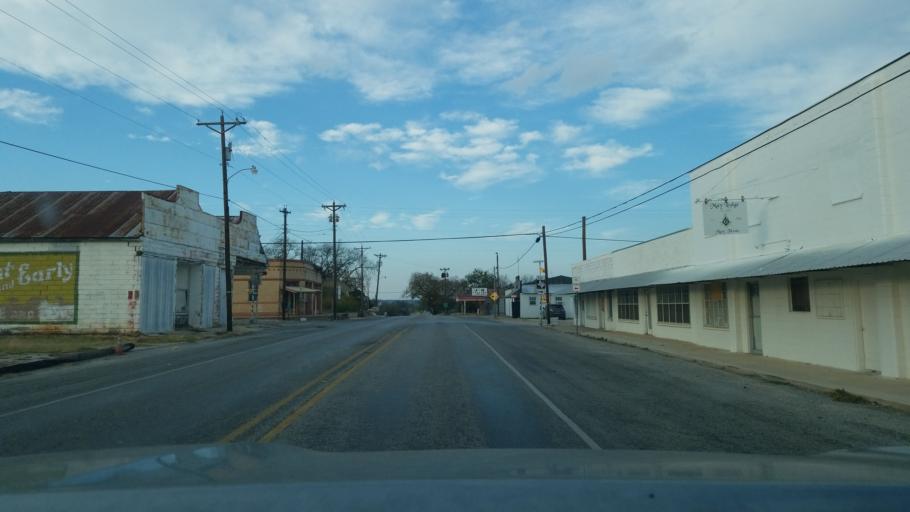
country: US
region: Texas
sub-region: Brown County
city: Lake Brownwood
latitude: 31.9789
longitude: -98.9204
